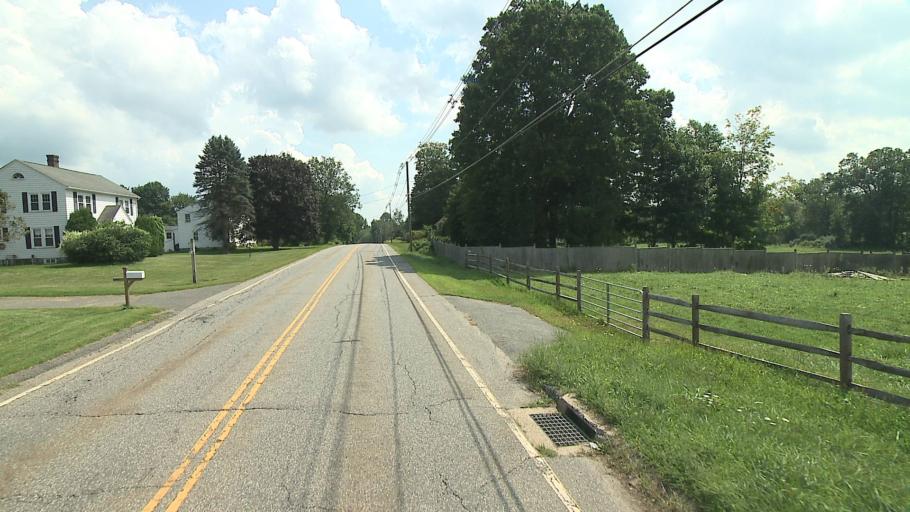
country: US
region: Connecticut
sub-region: Litchfield County
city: Bethlehem Village
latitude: 41.6858
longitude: -73.1718
